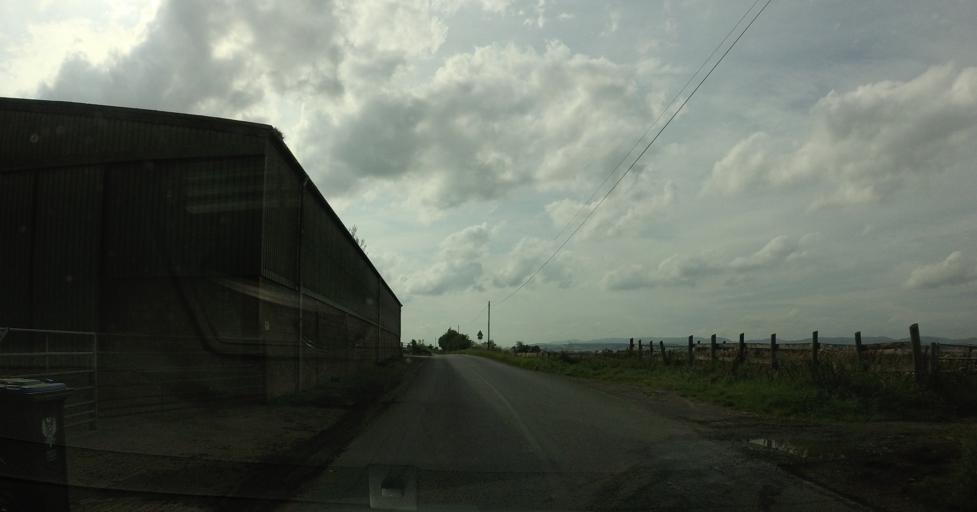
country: GB
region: Scotland
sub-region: Perth and Kinross
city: Methven
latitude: 56.3942
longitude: -3.5573
